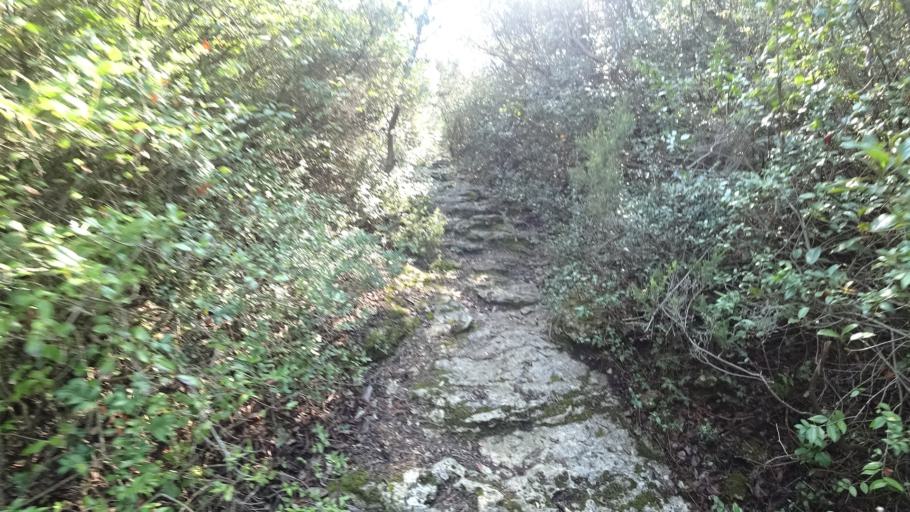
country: HR
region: Primorsko-Goranska
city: Mali Losinj
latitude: 44.5013
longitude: 14.5235
